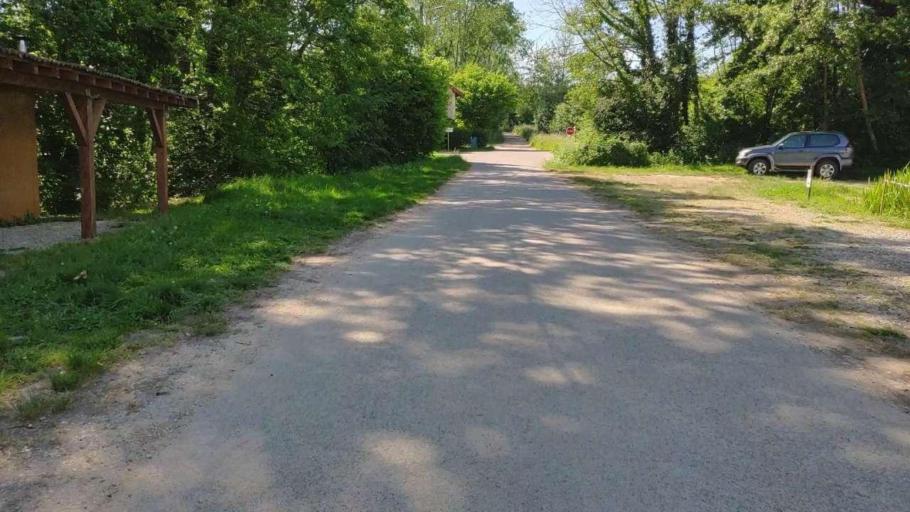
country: FR
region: Franche-Comte
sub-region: Departement du Jura
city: Bletterans
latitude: 46.7664
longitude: 5.4599
